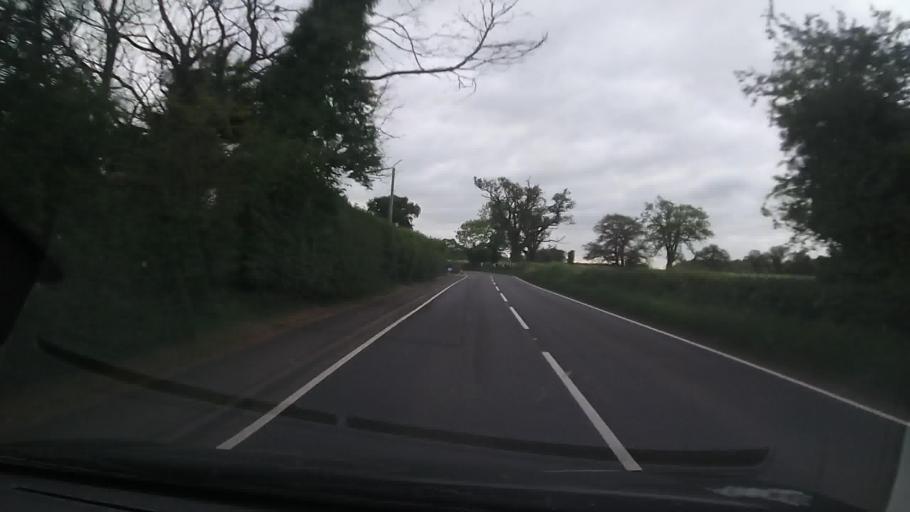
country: GB
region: England
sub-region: Shropshire
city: Clive
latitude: 52.7699
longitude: -2.7506
